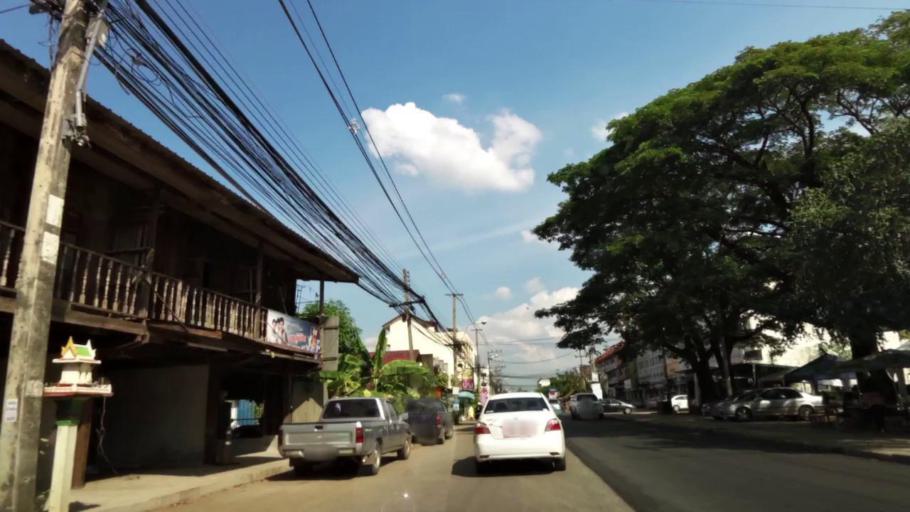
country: TH
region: Phrae
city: Phrae
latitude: 18.1361
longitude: 100.1427
